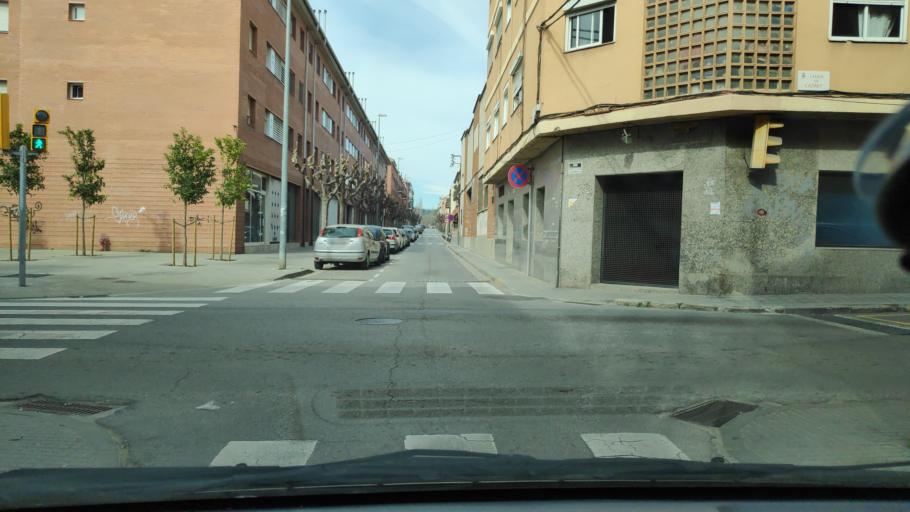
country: ES
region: Catalonia
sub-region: Provincia de Barcelona
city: Rubi
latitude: 41.4943
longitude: 2.0303
